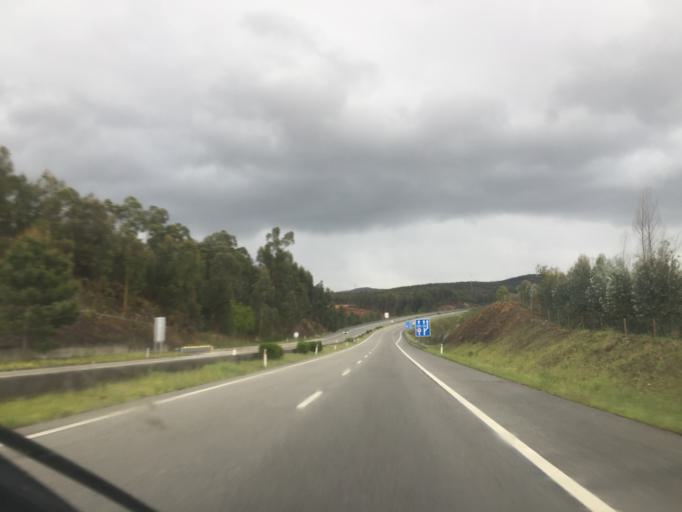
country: PT
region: Aveiro
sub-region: Agueda
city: Valongo
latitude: 40.6668
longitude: -8.4028
